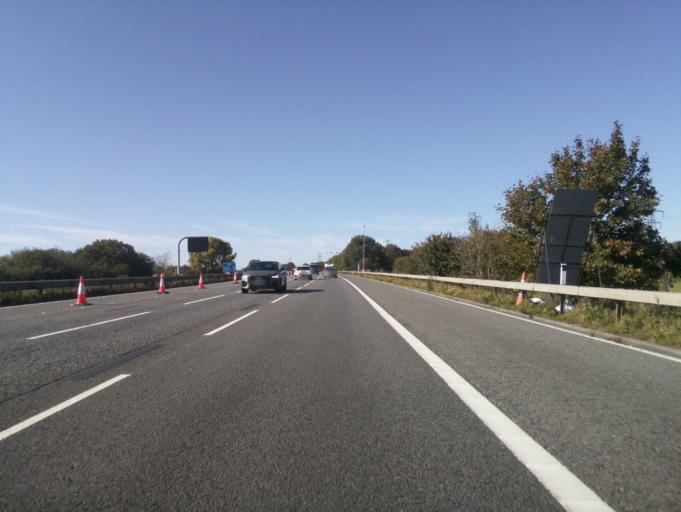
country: GB
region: England
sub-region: Wiltshire
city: Lydiard Tregoze
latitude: 51.5502
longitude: -1.8652
